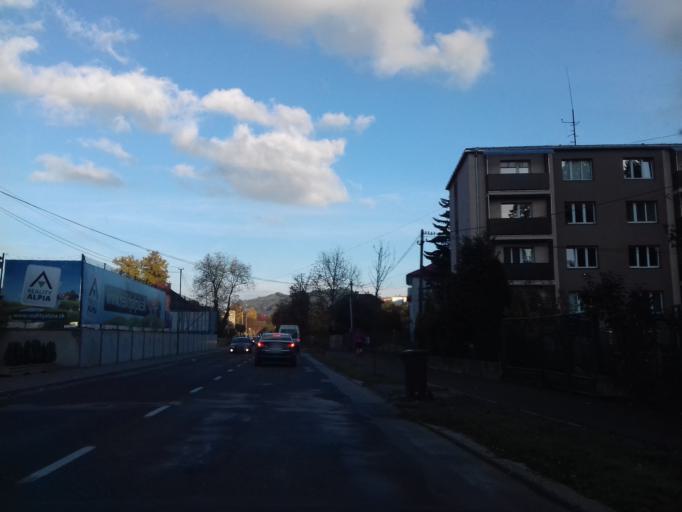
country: SK
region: Zilinsky
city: Ruzomberok
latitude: 49.0814
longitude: 19.2845
